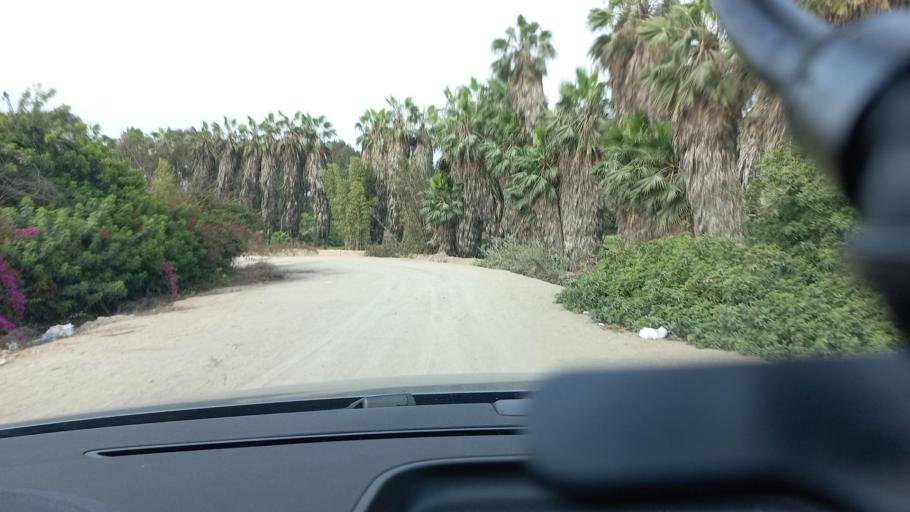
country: PE
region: Lima
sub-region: Lima
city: Punta Hermosa
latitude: -12.2643
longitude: -76.9071
